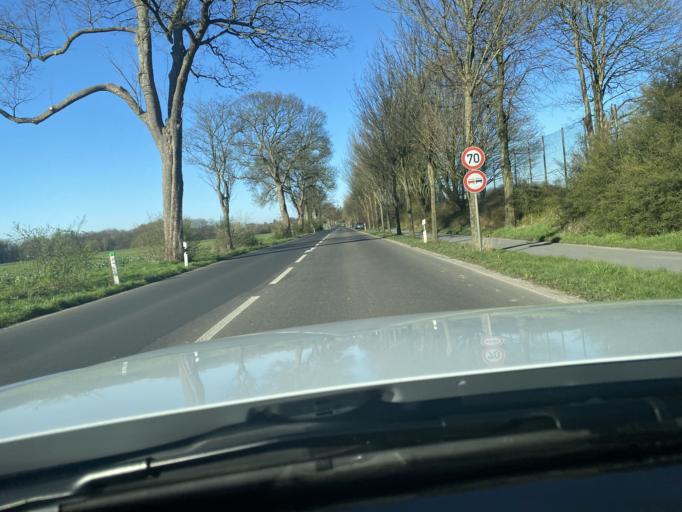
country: DE
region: North Rhine-Westphalia
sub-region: Regierungsbezirk Dusseldorf
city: Erkrath
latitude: 51.2611
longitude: 6.9005
